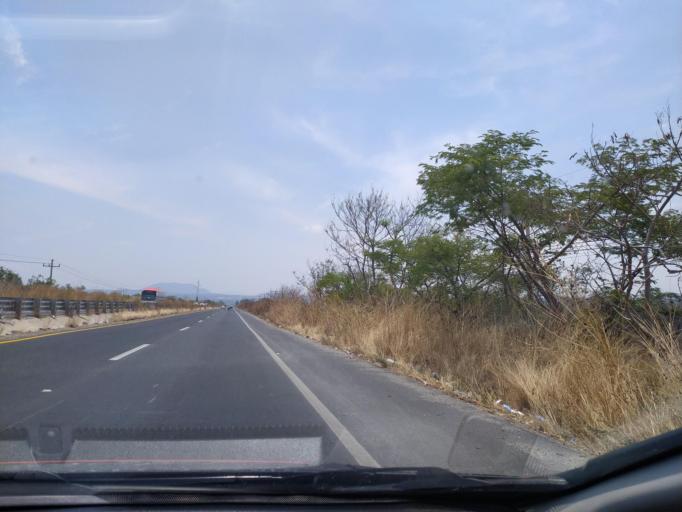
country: MX
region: Jalisco
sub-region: Acatlan de Juarez
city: Villa de los Ninos
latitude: 20.3770
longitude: -103.5926
